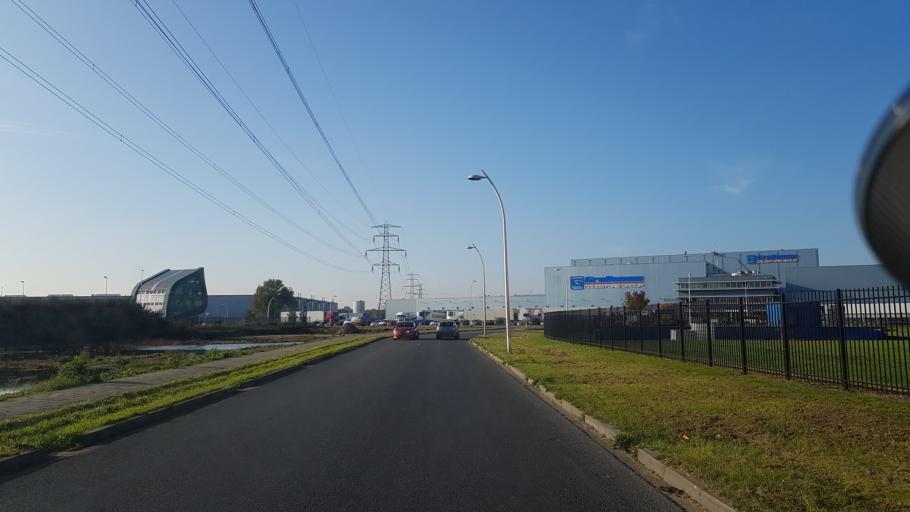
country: NL
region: Gelderland
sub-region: Gemeente Apeldoorn
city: Apeldoorn
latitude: 52.1983
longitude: 6.0317
